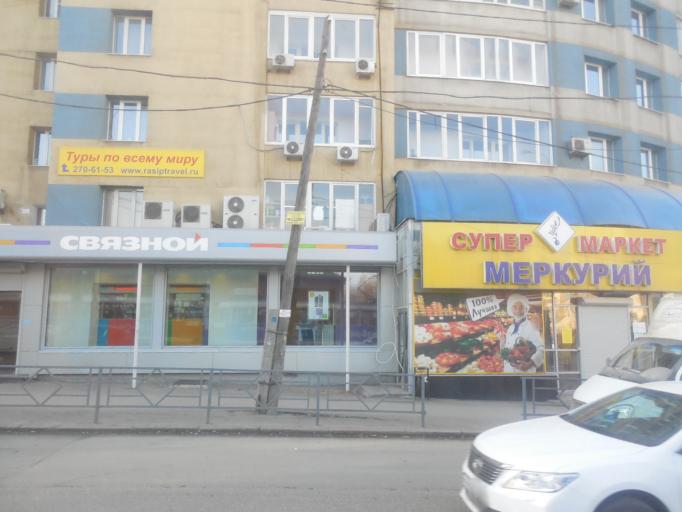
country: RU
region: Samara
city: Samara
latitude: 53.2028
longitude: 50.1266
